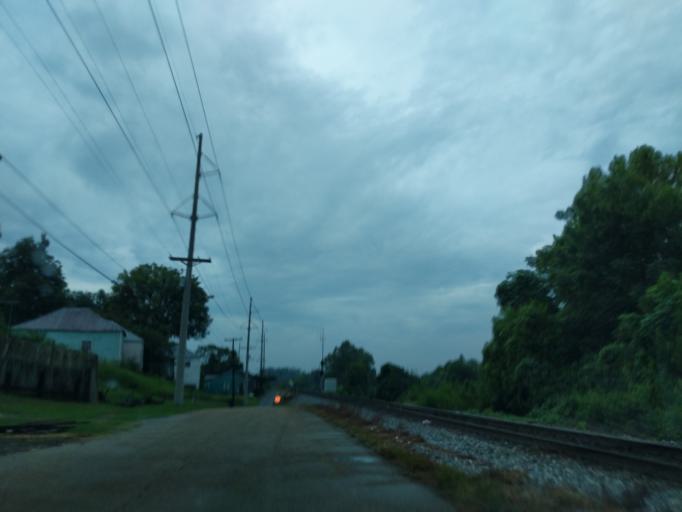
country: US
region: Mississippi
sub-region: Warren County
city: Vicksburg
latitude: 32.3384
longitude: -90.8890
